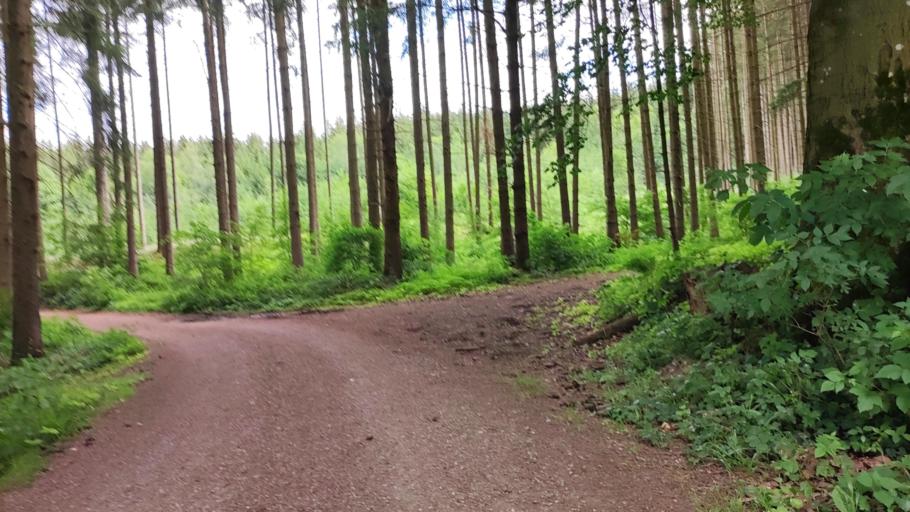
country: DE
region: Bavaria
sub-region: Swabia
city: Horgau
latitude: 48.4101
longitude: 10.6950
